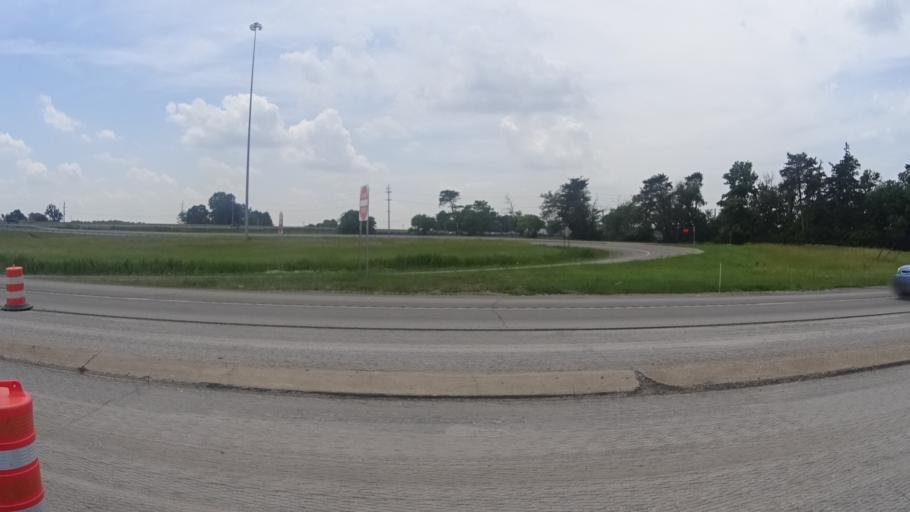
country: US
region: Ohio
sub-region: Erie County
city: Milan
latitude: 41.3250
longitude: -82.6181
